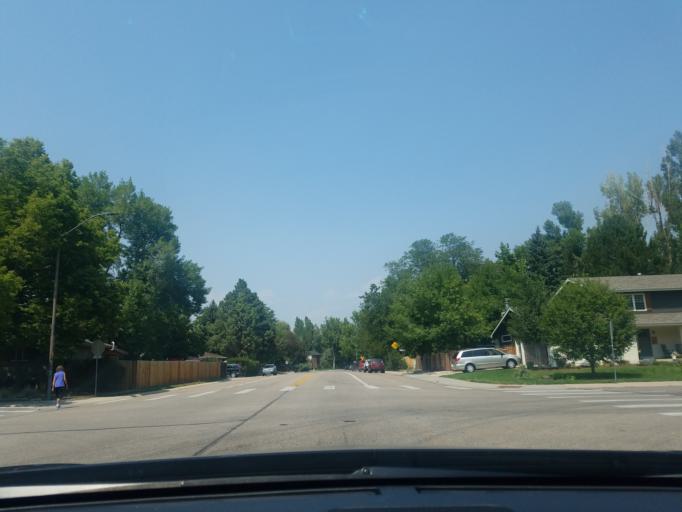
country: US
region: Colorado
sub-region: Larimer County
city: Fort Collins
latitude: 40.5577
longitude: -105.0675
